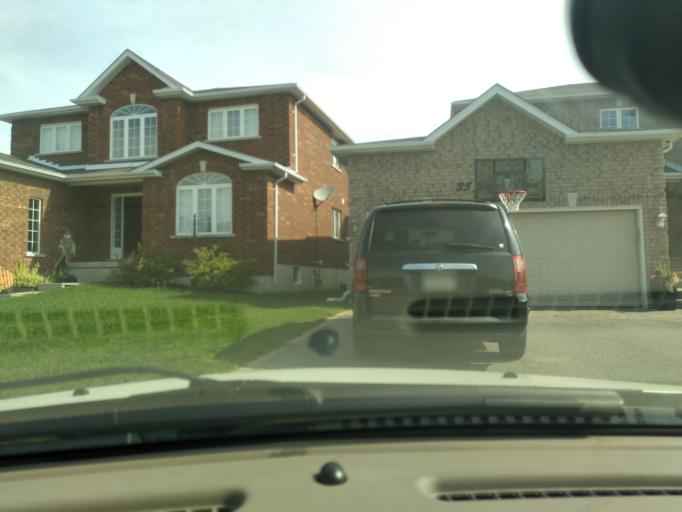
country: CA
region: Ontario
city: Barrie
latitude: 44.3781
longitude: -79.7277
